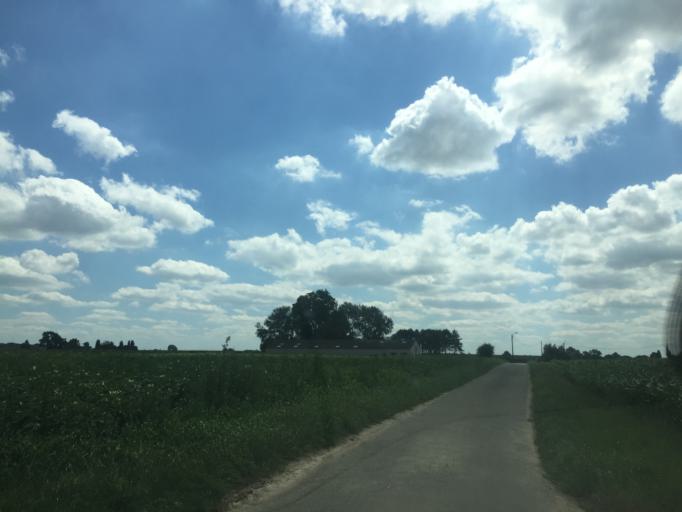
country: BE
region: Flanders
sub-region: Provincie West-Vlaanderen
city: Kortemark
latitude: 50.9980
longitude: 3.0420
